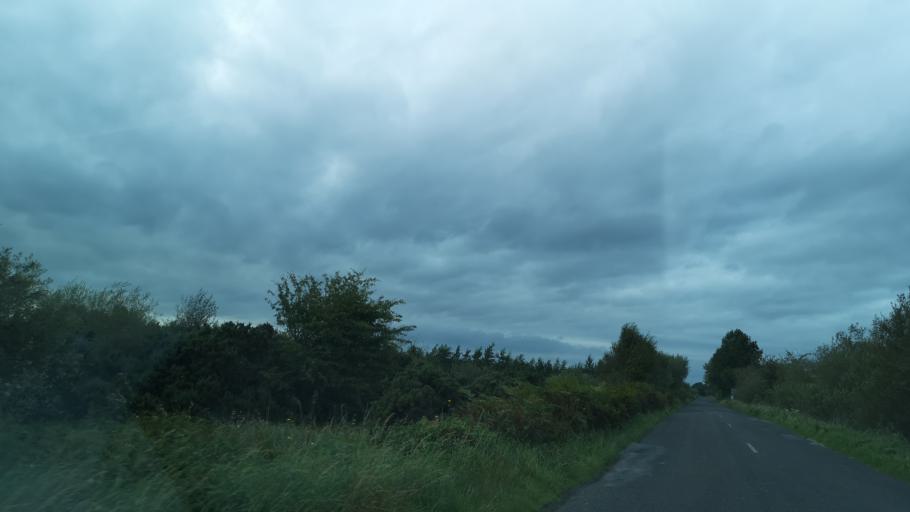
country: IE
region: Leinster
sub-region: Uibh Fhaili
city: Ferbane
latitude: 53.2110
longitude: -7.7885
